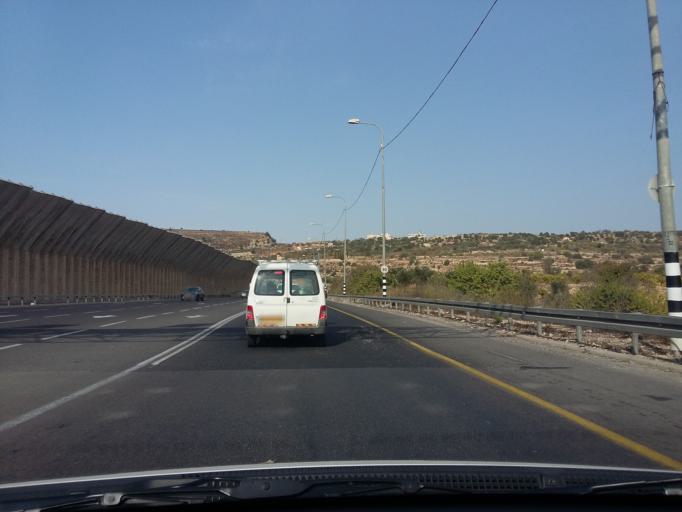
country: PS
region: West Bank
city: Al Khadir
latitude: 31.7055
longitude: 35.1658
